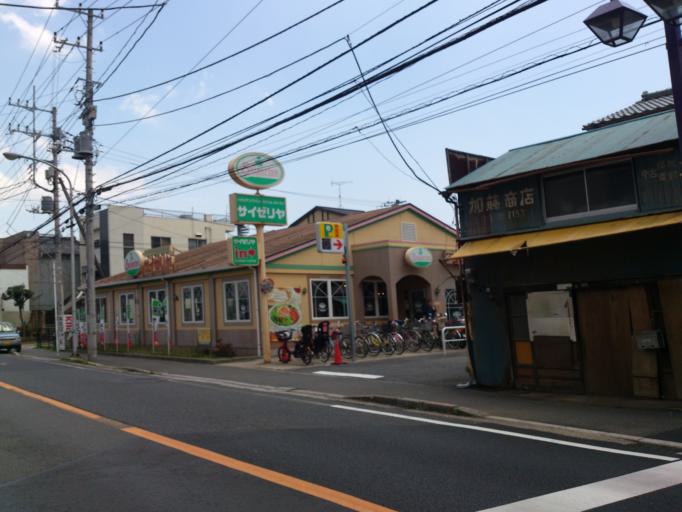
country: JP
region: Chiba
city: Funabashi
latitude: 35.7157
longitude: 139.9456
